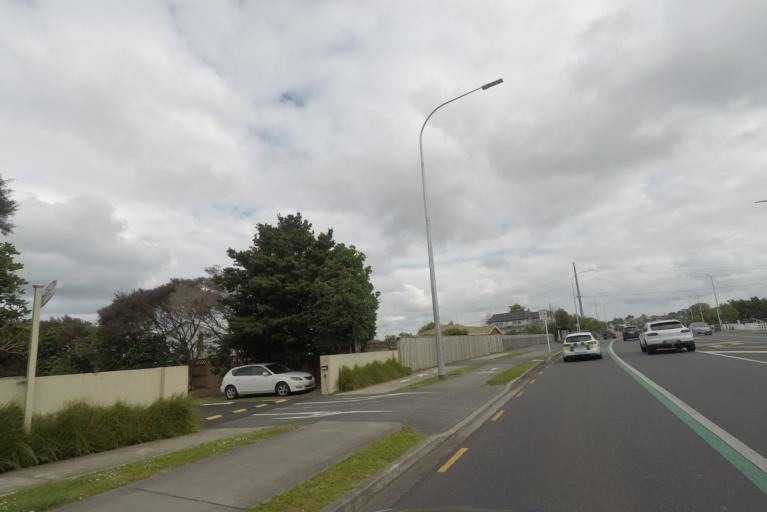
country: NZ
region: Auckland
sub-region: Auckland
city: Rothesay Bay
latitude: -36.7381
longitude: 174.6922
